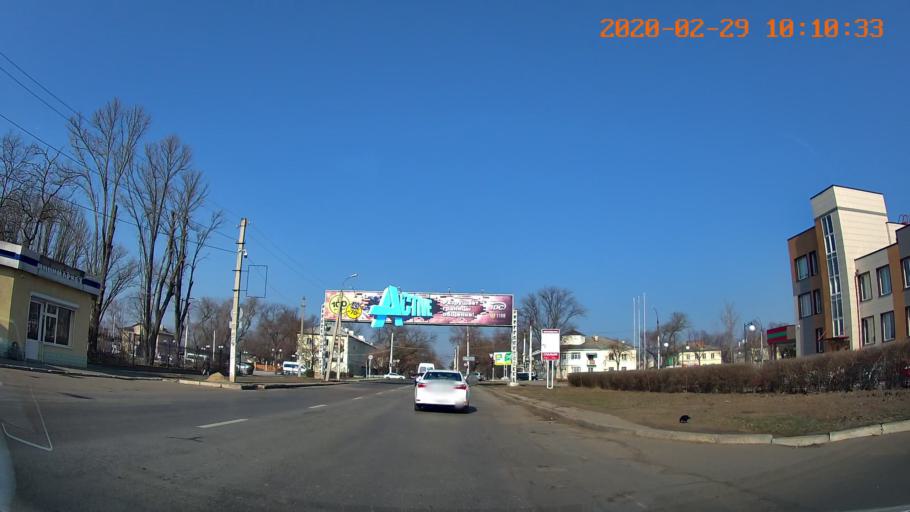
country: MD
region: Telenesti
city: Tiraspolul Nou
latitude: 46.8335
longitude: 29.6435
